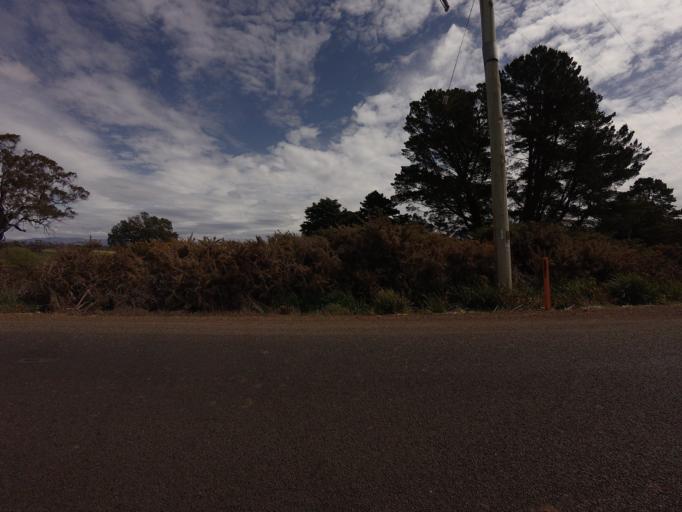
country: AU
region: Tasmania
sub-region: Northern Midlands
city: Longford
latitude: -41.7179
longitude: 147.1869
